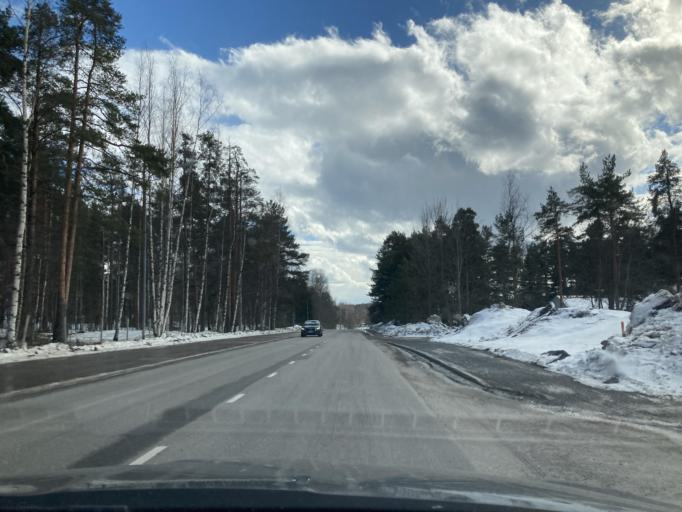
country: FI
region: Paijanne Tavastia
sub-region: Lahti
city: Heinola
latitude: 61.2073
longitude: 26.0446
